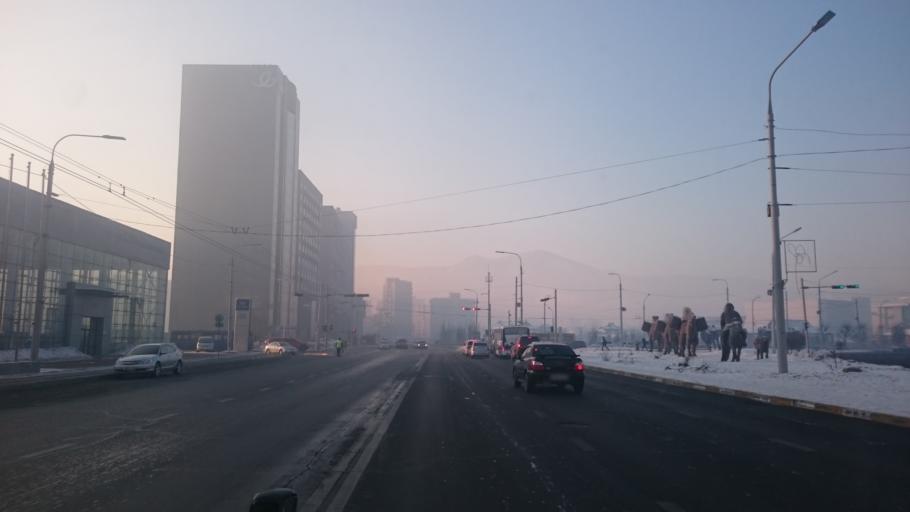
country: MN
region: Ulaanbaatar
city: Ulaanbaatar
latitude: 47.9002
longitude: 106.9096
